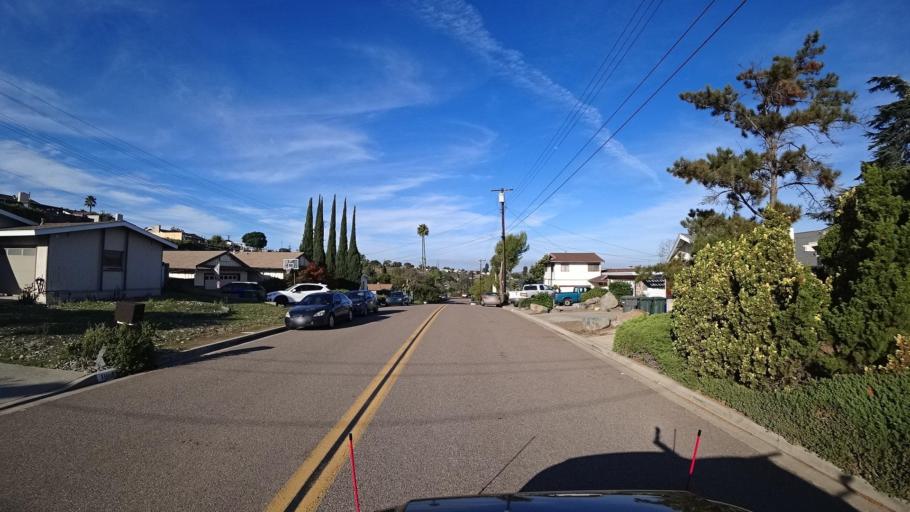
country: US
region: California
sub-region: San Diego County
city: Spring Valley
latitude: 32.7410
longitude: -116.9762
